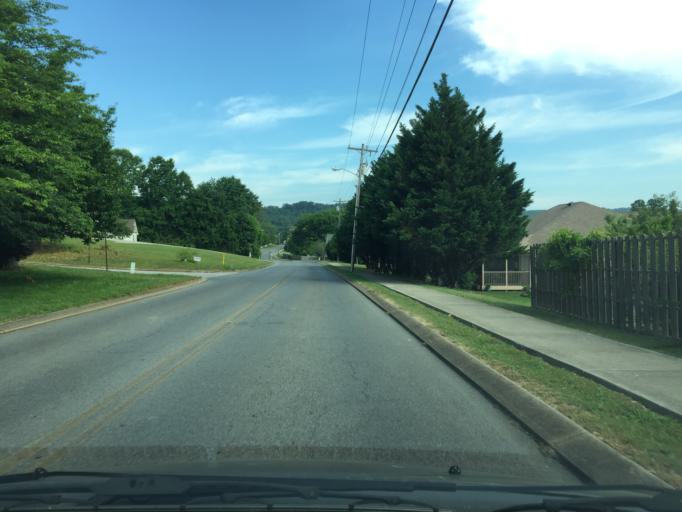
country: US
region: Tennessee
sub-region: Hamilton County
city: Collegedale
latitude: 35.0626
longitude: -85.0340
